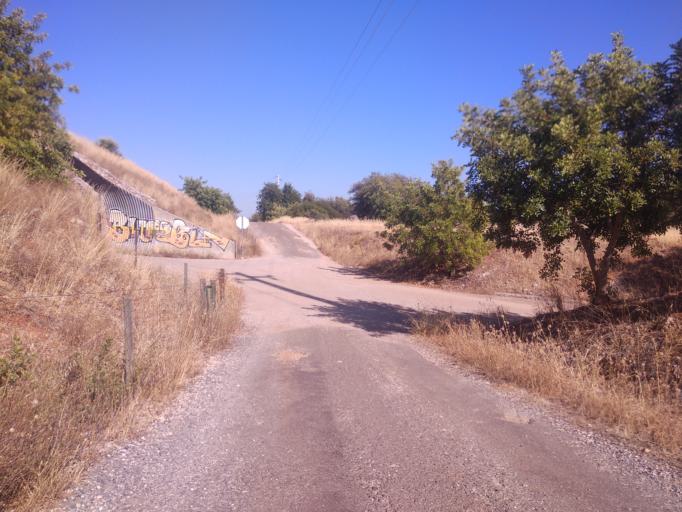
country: PT
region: Faro
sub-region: Sao Bras de Alportel
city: Sao Bras de Alportel
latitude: 37.1475
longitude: -7.9084
